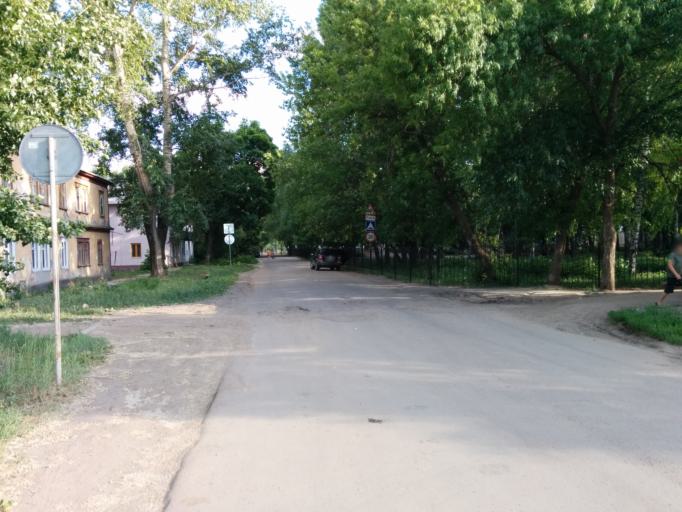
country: RU
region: Tambov
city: Tambov
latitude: 52.7482
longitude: 41.4410
